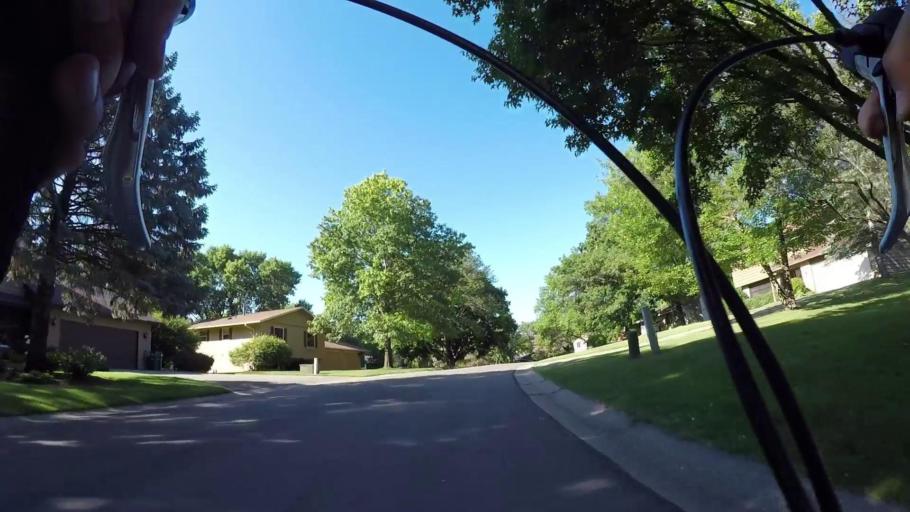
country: US
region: Minnesota
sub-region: Carver County
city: Chanhassen
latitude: 44.8754
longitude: -93.5101
